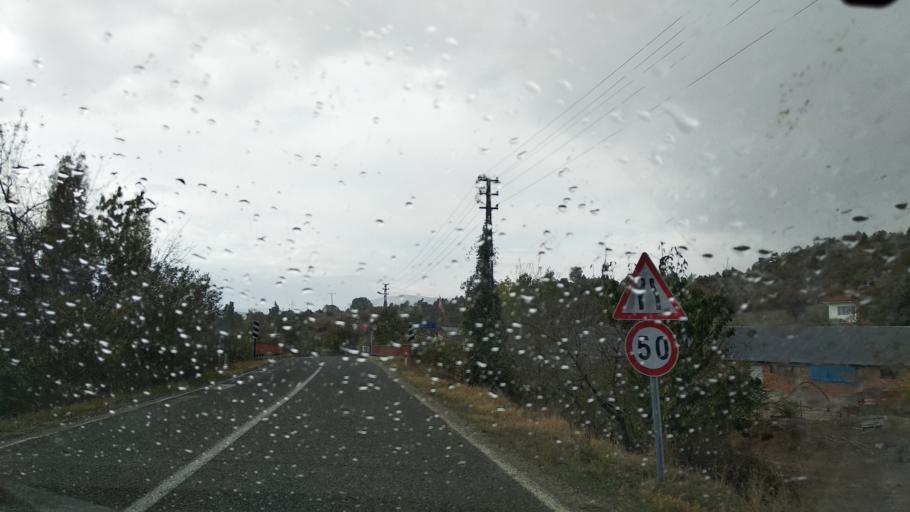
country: TR
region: Ankara
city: Nallihan
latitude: 40.3336
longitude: 31.4142
